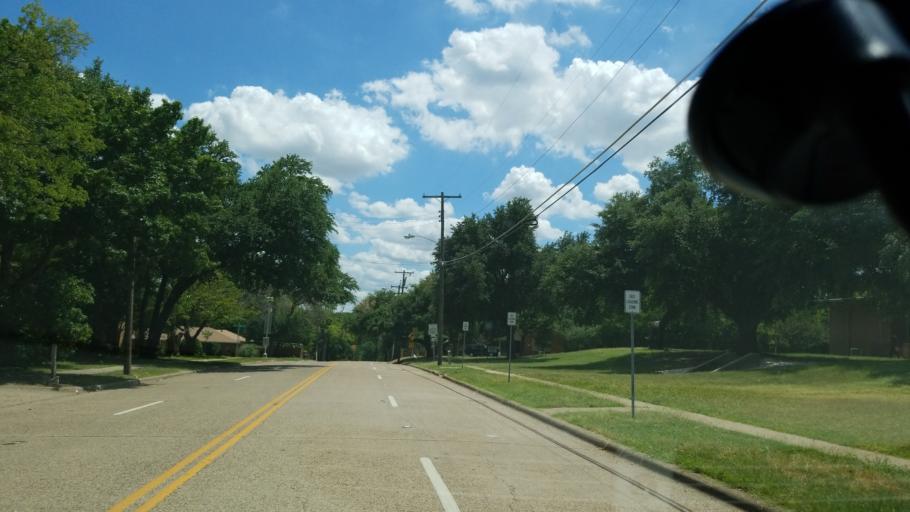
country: US
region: Texas
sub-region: Dallas County
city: Cockrell Hill
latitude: 32.6968
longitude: -96.8602
